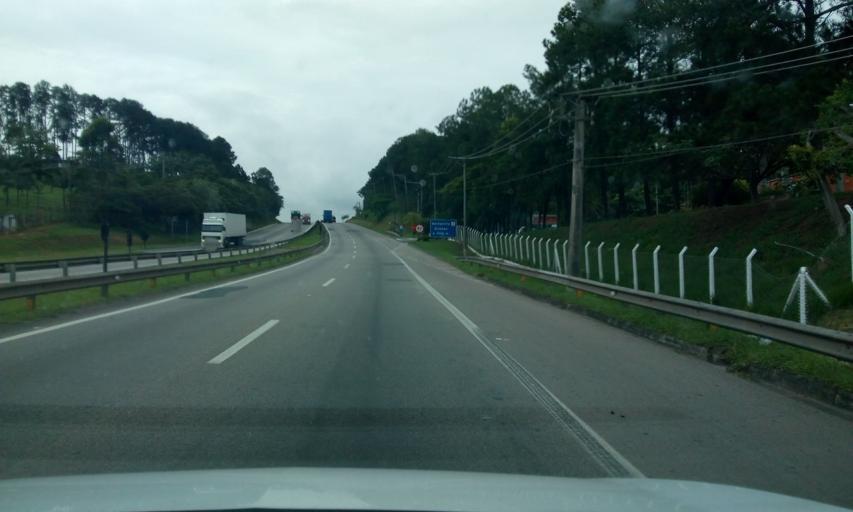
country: BR
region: Sao Paulo
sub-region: Jundiai
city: Jundiai
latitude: -23.1813
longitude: -46.9636
